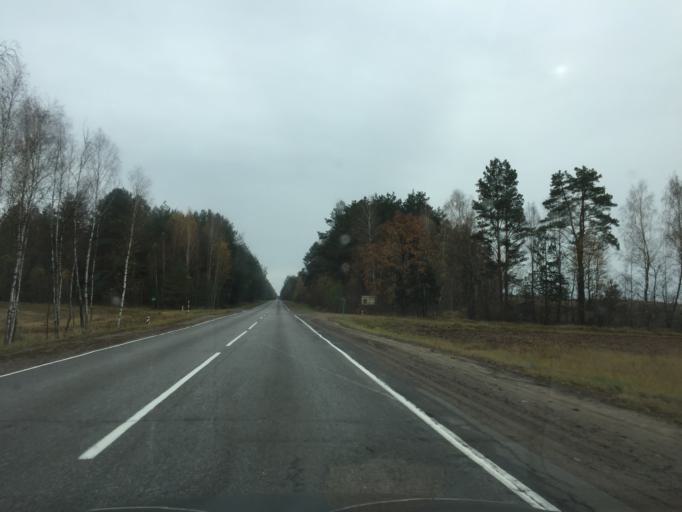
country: BY
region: Mogilev
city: Chavusy
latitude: 53.7625
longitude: 31.0672
